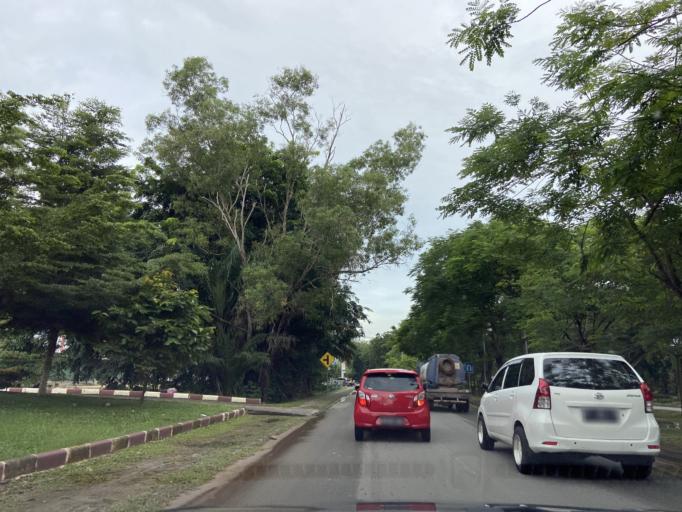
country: SG
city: Singapore
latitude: 1.1108
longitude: 103.9483
